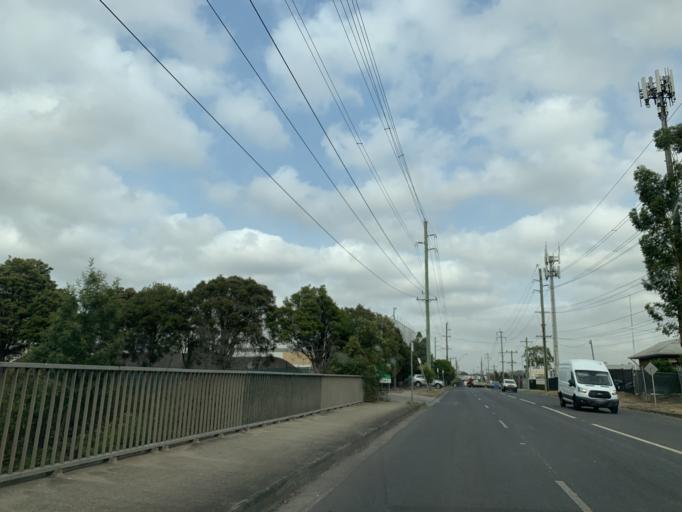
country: AU
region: New South Wales
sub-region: Holroyd
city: Girraween
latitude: -33.7747
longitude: 150.9502
